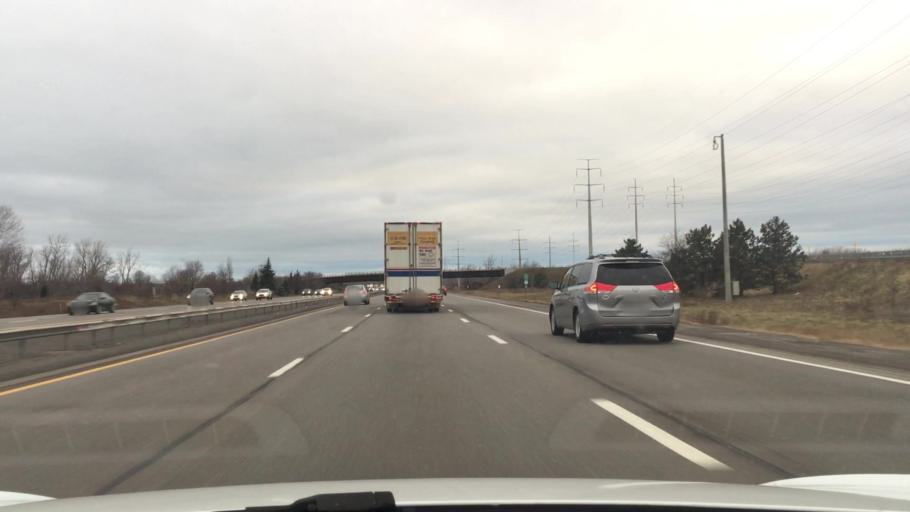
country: US
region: New York
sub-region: Erie County
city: Amherst
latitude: 42.9948
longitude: -78.8043
